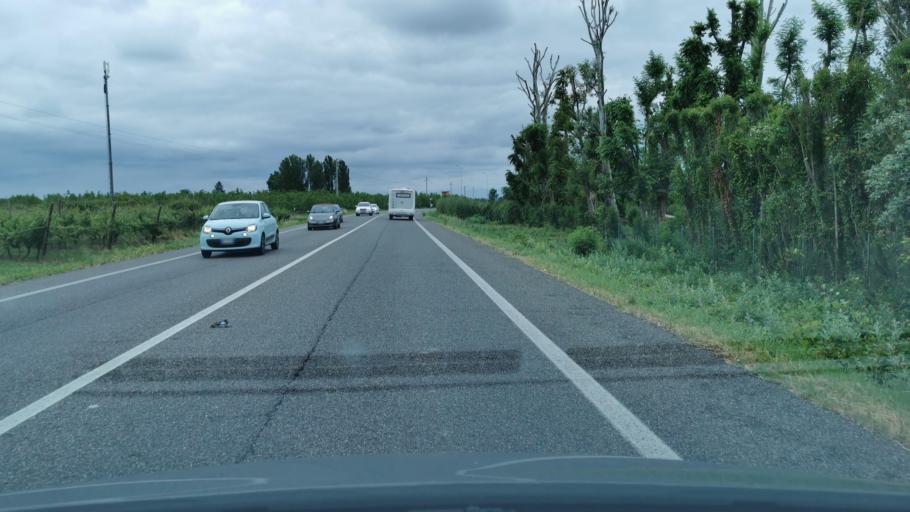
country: IT
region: Emilia-Romagna
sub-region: Provincia di Ravenna
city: Granarolo
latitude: 44.3528
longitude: 11.9275
